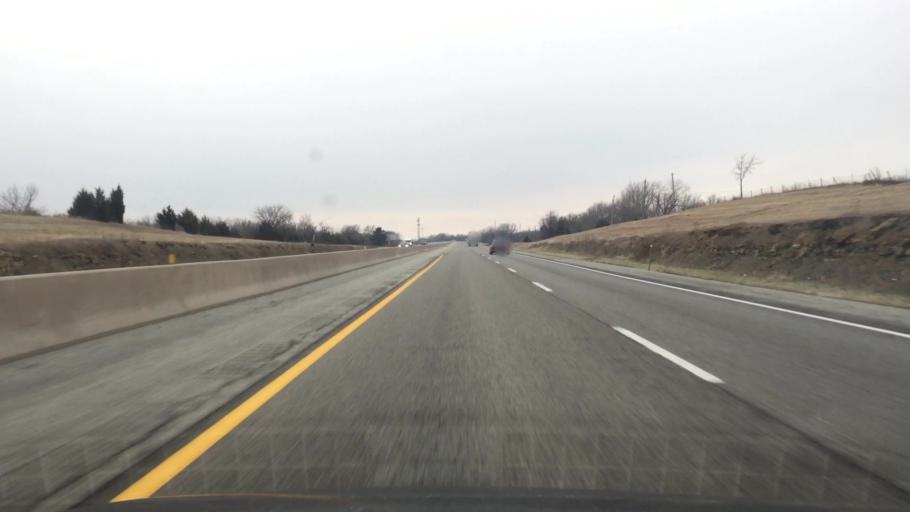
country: US
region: Kansas
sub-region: Shawnee County
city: Topeka
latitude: 39.0117
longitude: -95.6452
